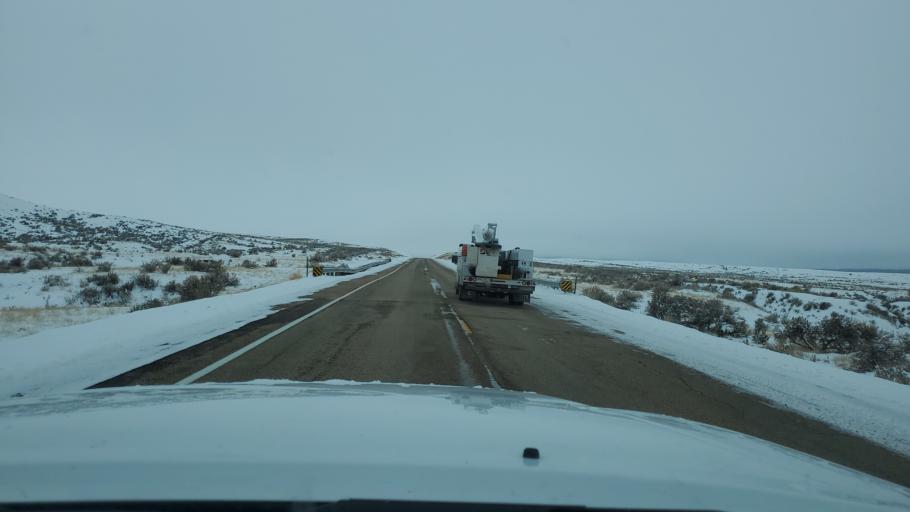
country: US
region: Colorado
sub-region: Rio Blanco County
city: Rangely
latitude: 40.2955
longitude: -108.5349
